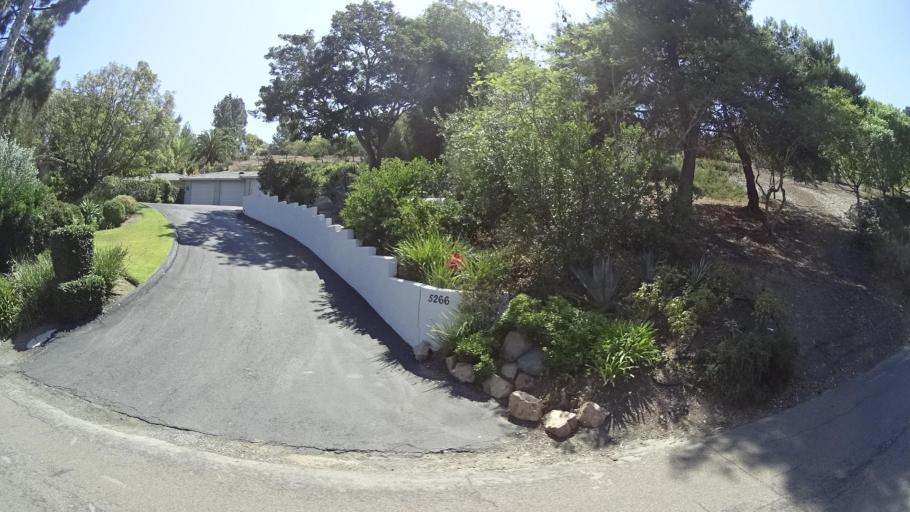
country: US
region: California
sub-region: San Diego County
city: Rancho Santa Fe
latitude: 33.0208
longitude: -117.2242
